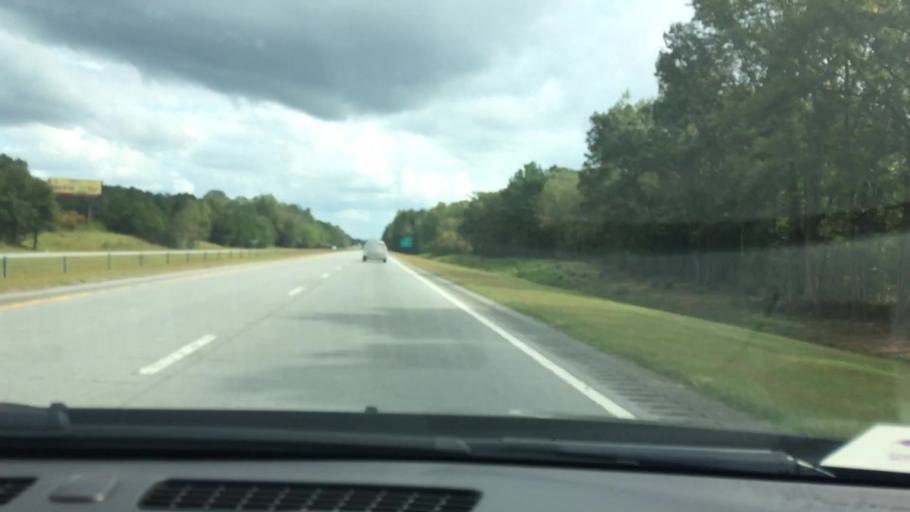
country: US
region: North Carolina
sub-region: Pitt County
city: Farmville
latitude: 35.6199
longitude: -77.6947
